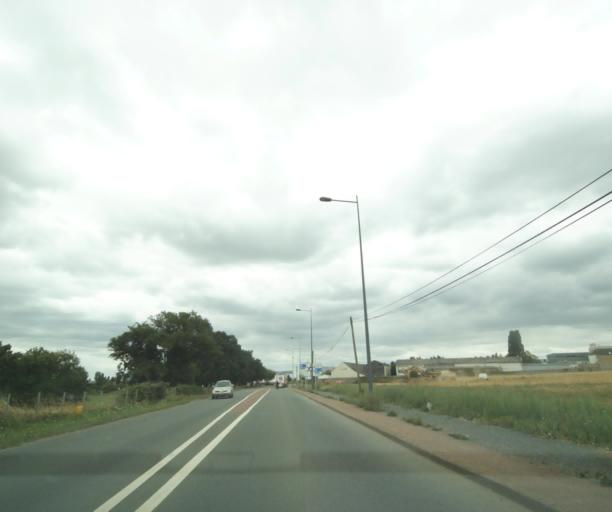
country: FR
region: Pays de la Loire
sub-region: Departement de la Sarthe
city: Solesmes
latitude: 47.8296
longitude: -0.3076
